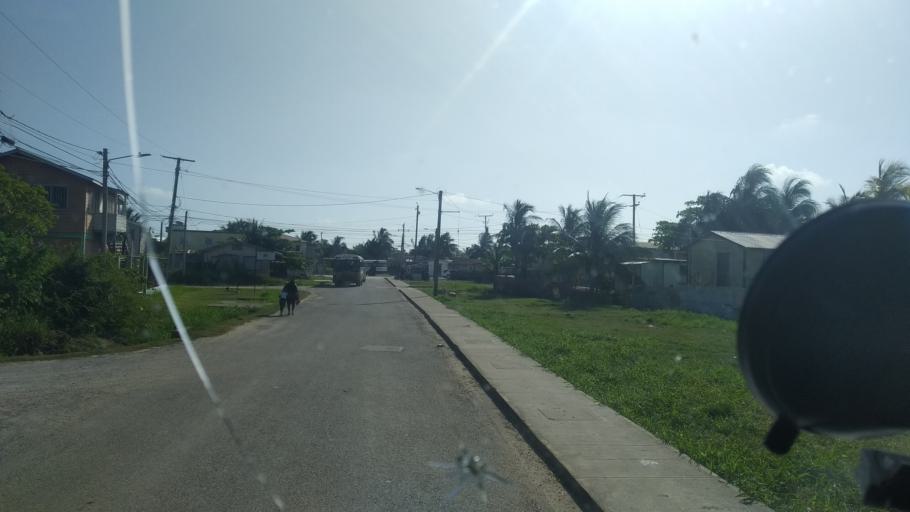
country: BZ
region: Belize
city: Belize City
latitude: 17.4848
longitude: -88.2033
